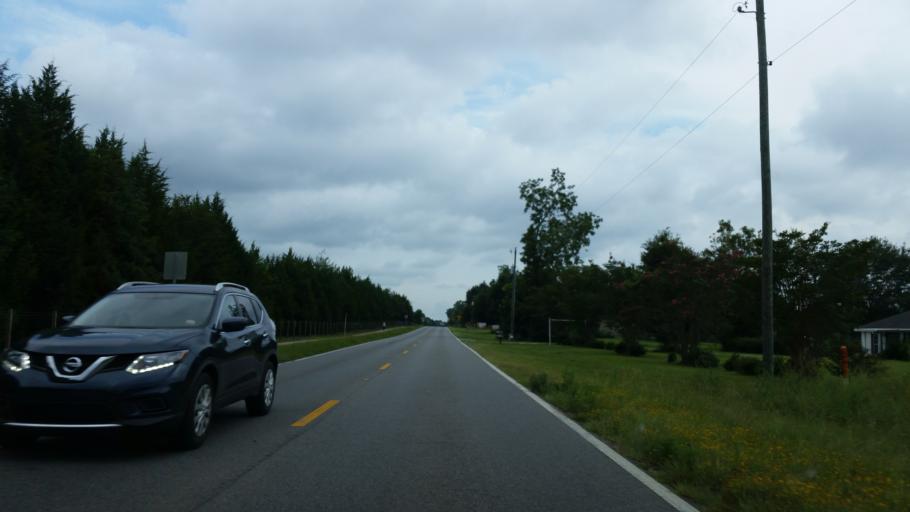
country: US
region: Florida
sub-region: Santa Rosa County
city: Pace
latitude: 30.6282
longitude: -87.1481
